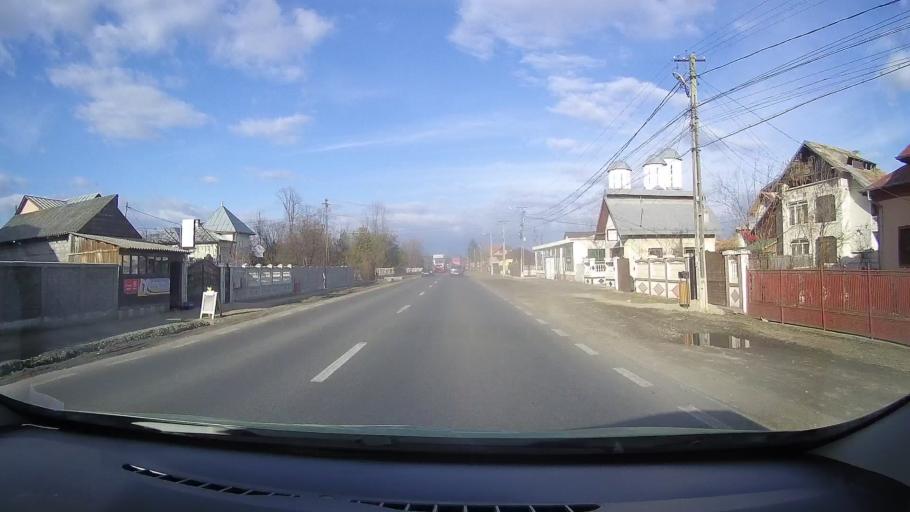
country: RO
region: Dambovita
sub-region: Comuna Ulmi
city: Viisoara
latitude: 44.8789
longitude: 25.4257
